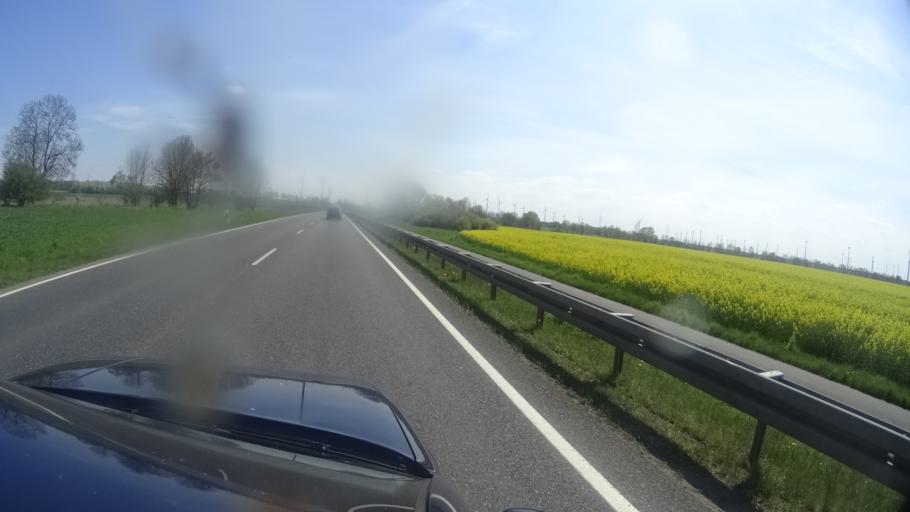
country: DE
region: Brandenburg
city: Nauen
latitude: 52.6081
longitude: 12.8445
